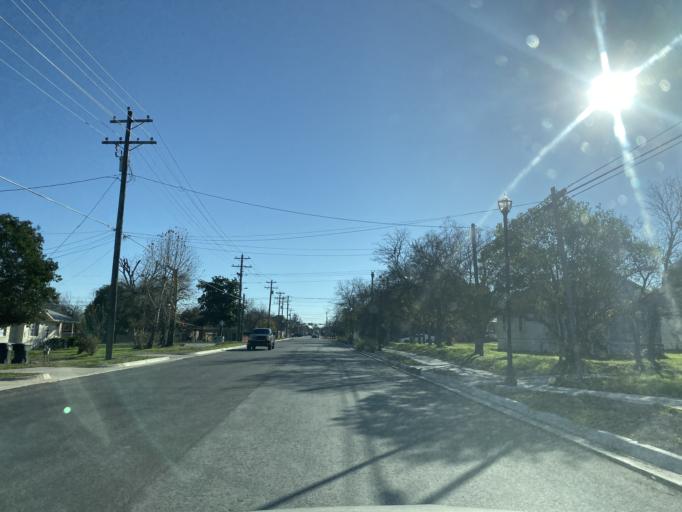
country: US
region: Texas
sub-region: Hays County
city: Kyle
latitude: 29.9913
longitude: -97.8768
